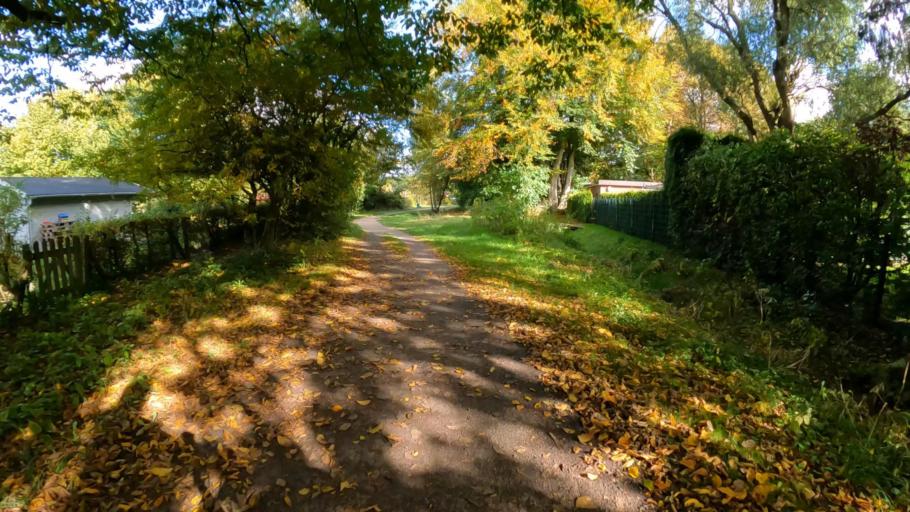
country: DE
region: Hamburg
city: Langenhorn
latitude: 53.6585
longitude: 9.9926
